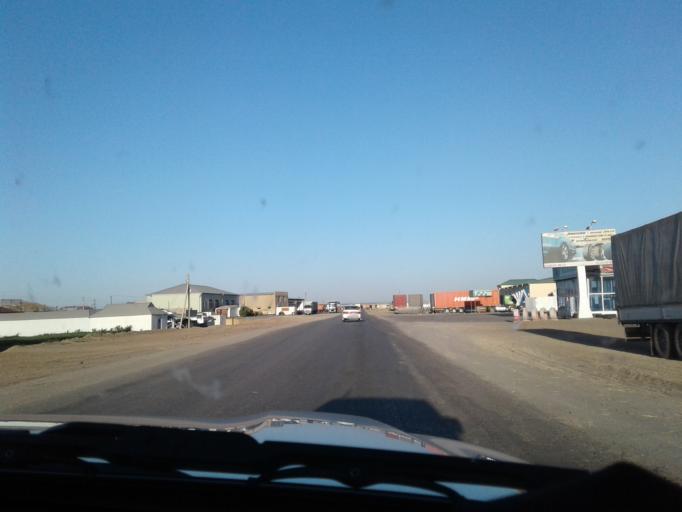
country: TM
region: Mary
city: Mary
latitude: 37.5654
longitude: 61.8166
